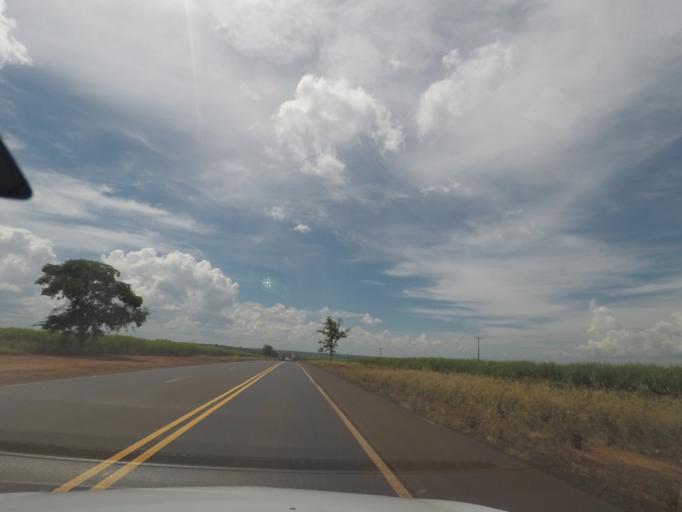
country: BR
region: Sao Paulo
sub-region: Barretos
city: Barretos
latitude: -20.2733
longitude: -48.6727
